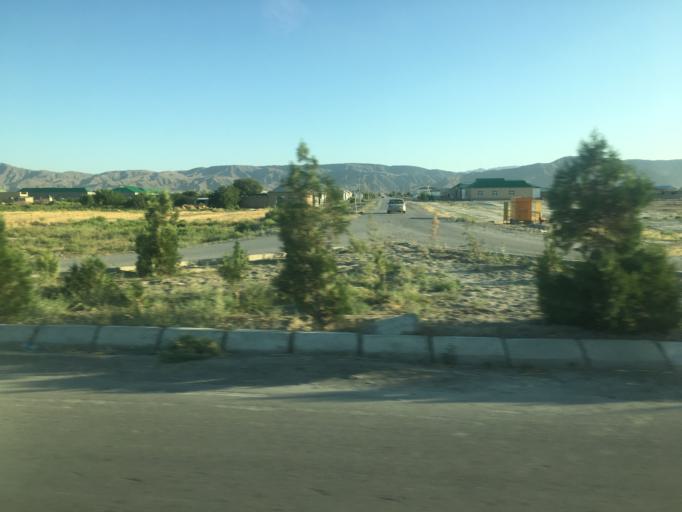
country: TM
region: Ahal
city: Baharly
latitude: 38.3147
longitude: 57.6063
